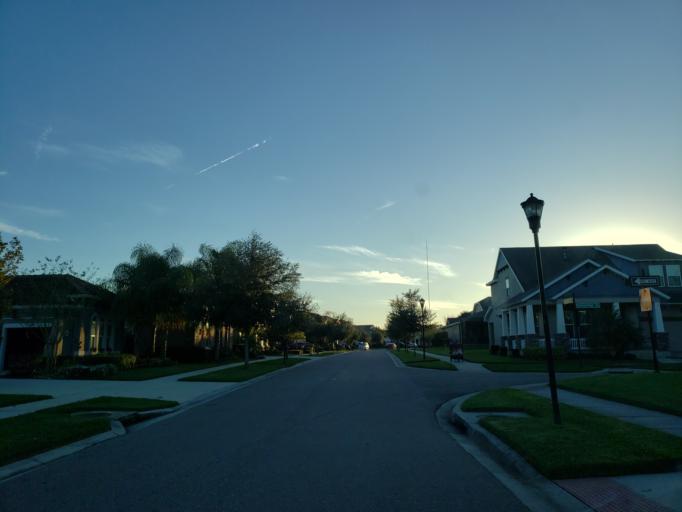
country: US
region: Florida
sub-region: Hillsborough County
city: Boyette
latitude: 27.8455
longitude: -82.2500
